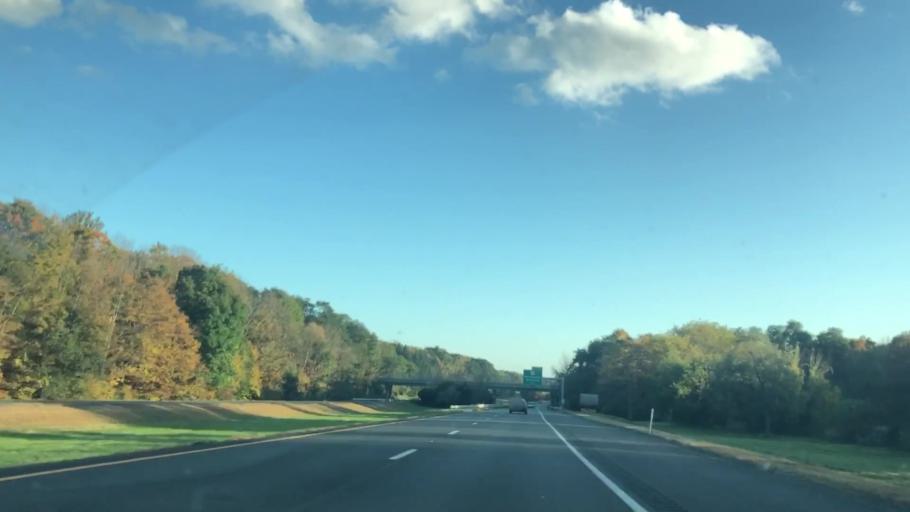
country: US
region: Massachusetts
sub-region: Franklin County
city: Bernardston
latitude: 42.6899
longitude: -72.5439
